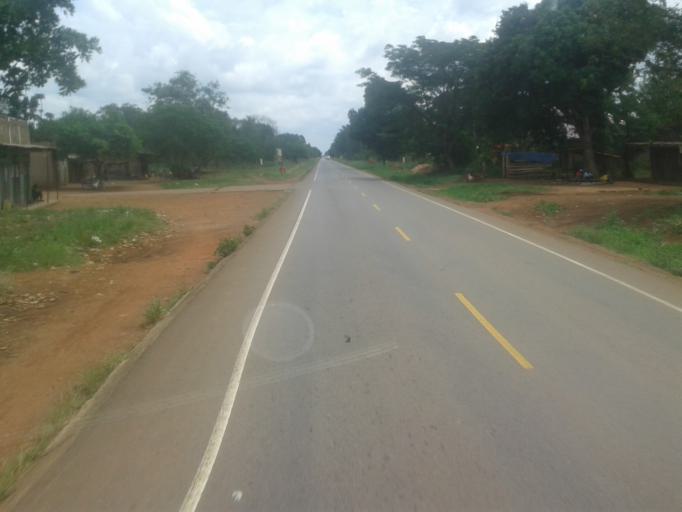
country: UG
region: Central Region
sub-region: Nakasongola District
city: Nakasongola
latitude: 1.0797
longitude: 32.4665
